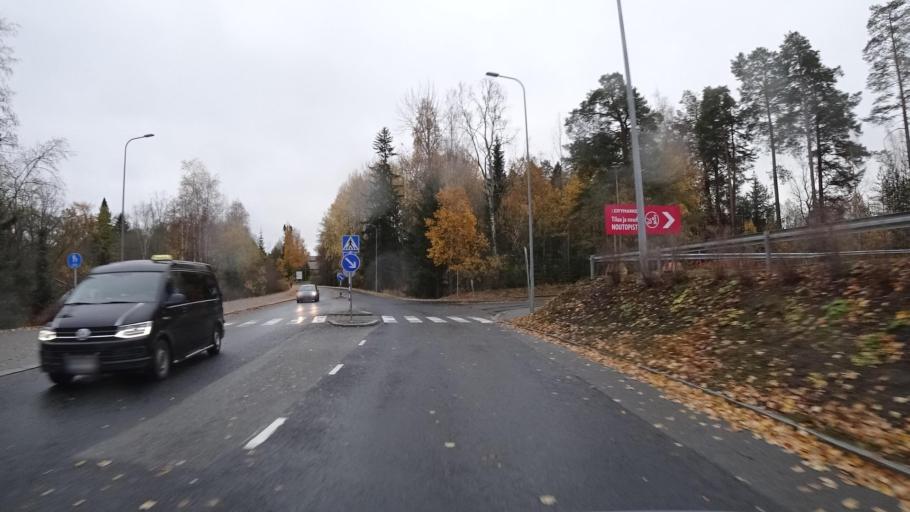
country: FI
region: Northern Savo
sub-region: Kuopio
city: Kuopio
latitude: 62.9317
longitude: 27.6784
